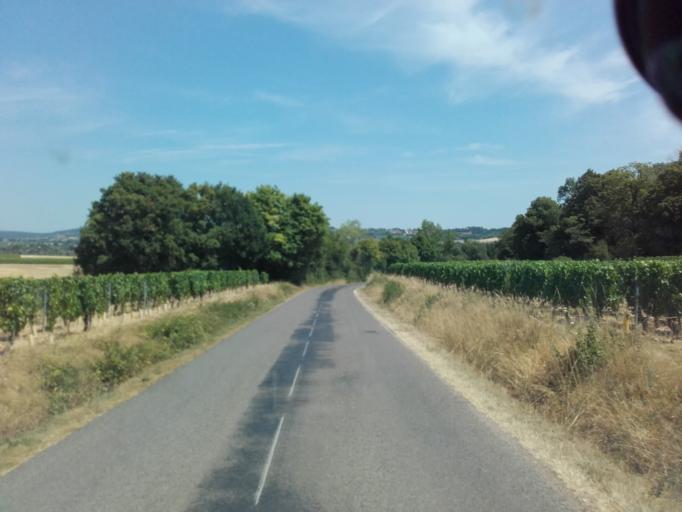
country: FR
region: Bourgogne
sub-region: Departement de Saone-et-Loire
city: Charnay-les-Macon
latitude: 46.2951
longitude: 4.7595
